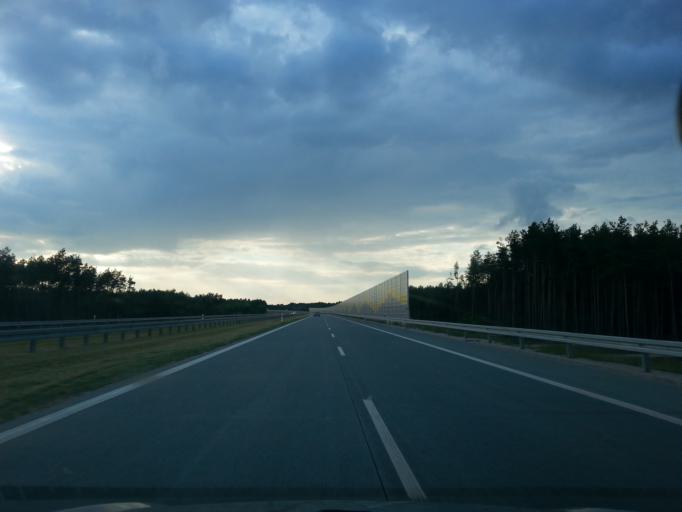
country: PL
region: Lodz Voivodeship
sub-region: Powiat zdunskowolski
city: Zdunska Wola
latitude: 51.5877
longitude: 18.8961
